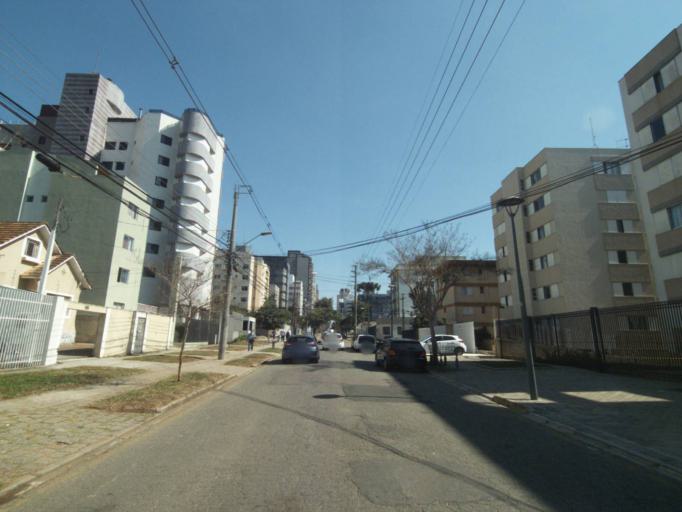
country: BR
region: Parana
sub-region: Curitiba
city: Curitiba
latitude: -25.4505
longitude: -49.2821
